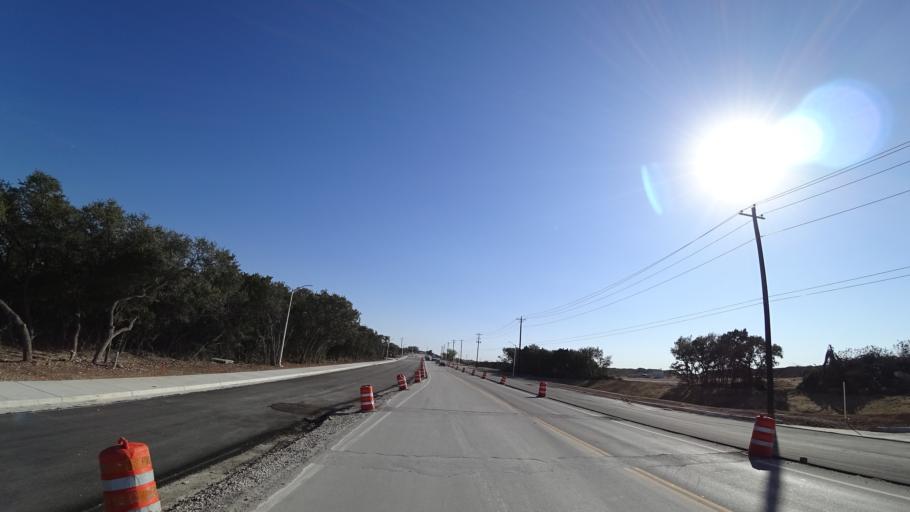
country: US
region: Texas
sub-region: Williamson County
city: Cedar Park
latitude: 30.5117
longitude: -97.8579
